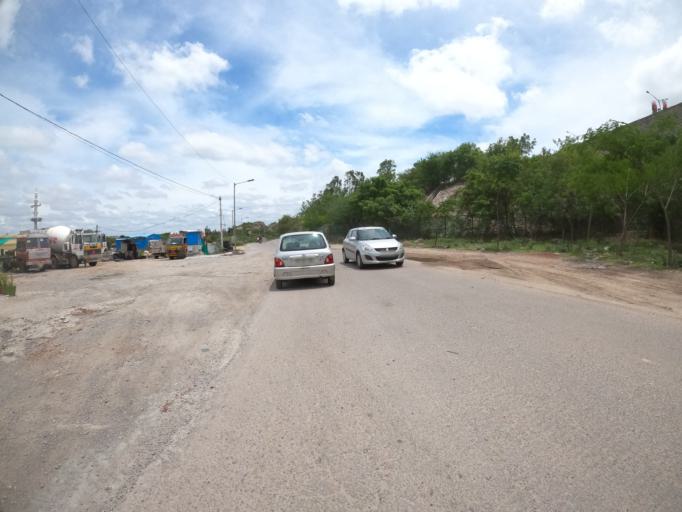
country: IN
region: Telangana
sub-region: Hyderabad
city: Hyderabad
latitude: 17.3091
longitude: 78.3768
